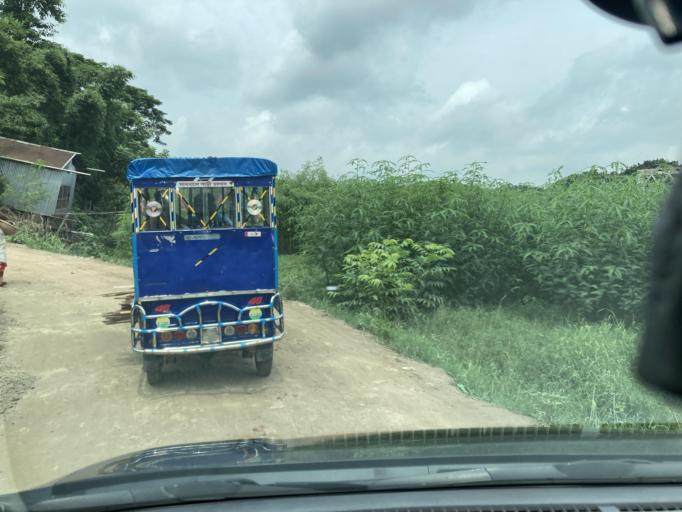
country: BD
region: Dhaka
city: Dohar
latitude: 23.7613
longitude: 90.1999
